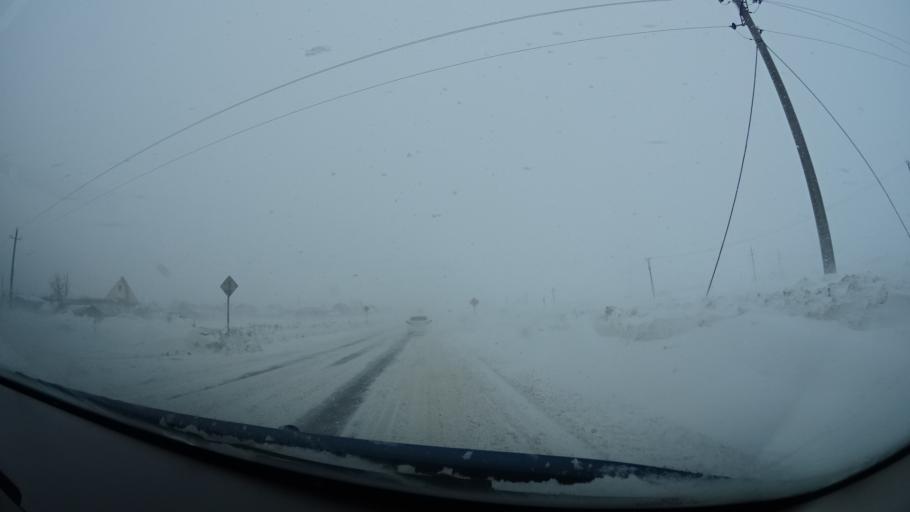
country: RU
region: Perm
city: Kuyeda
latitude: 56.4212
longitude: 55.5851
